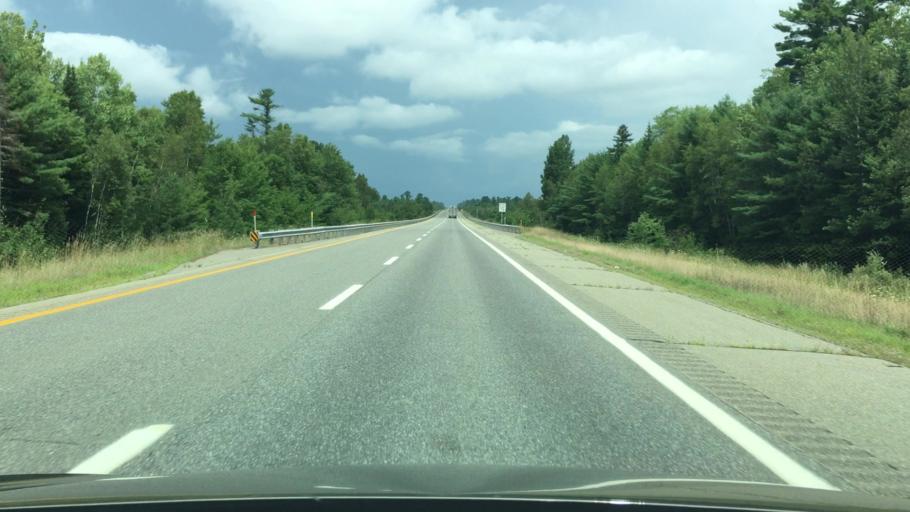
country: US
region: Maine
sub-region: Penobscot County
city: Lincoln
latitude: 45.3900
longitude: -68.6026
